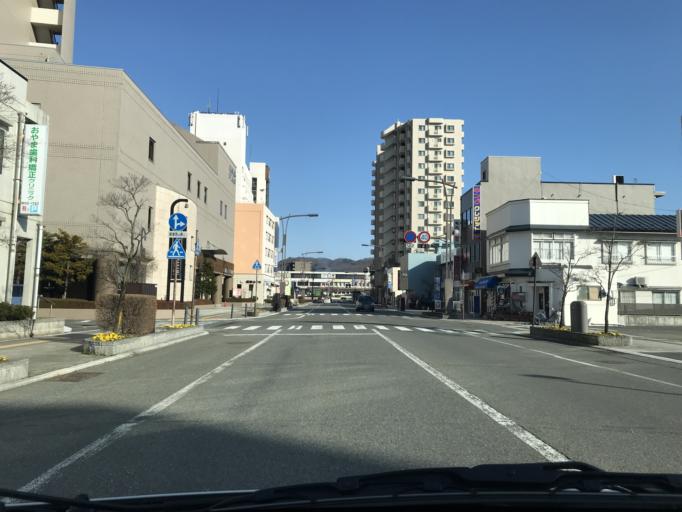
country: JP
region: Iwate
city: Kitakami
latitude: 39.2823
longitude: 141.1182
